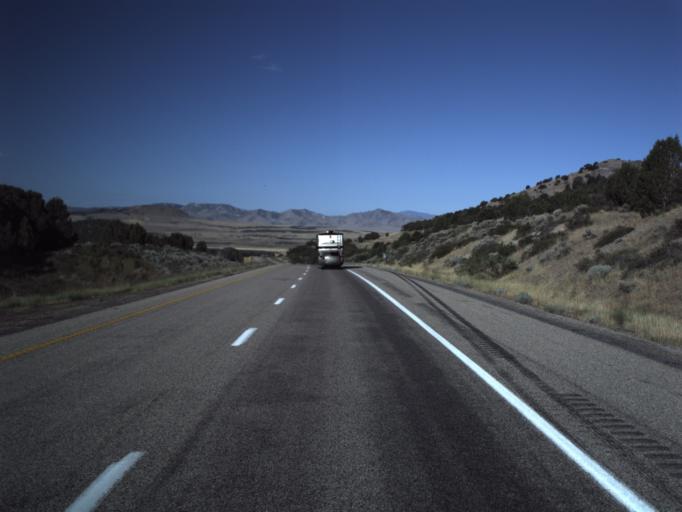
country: US
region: Utah
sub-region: Beaver County
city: Beaver
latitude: 38.6075
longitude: -112.5226
